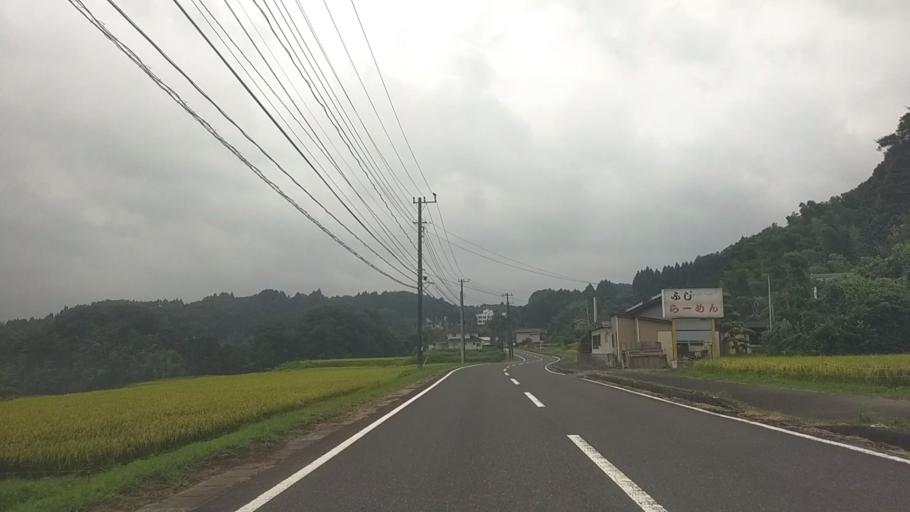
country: JP
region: Chiba
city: Kawaguchi
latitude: 35.2580
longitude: 140.0561
